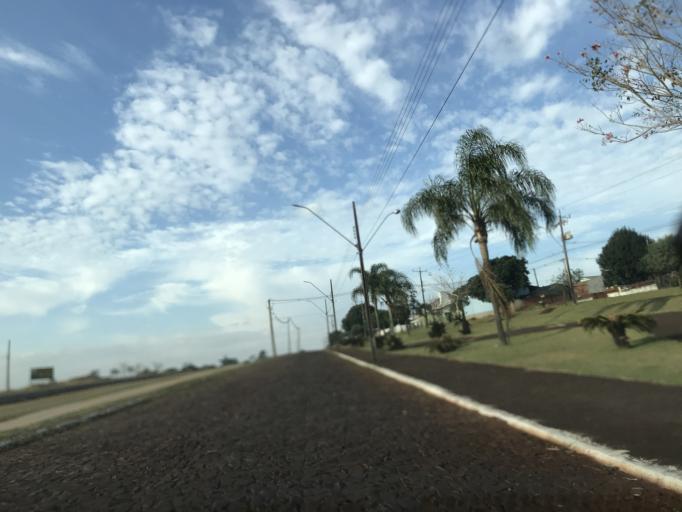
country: BR
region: Parana
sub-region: Cascavel
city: Cascavel
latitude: -25.0478
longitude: -53.6125
